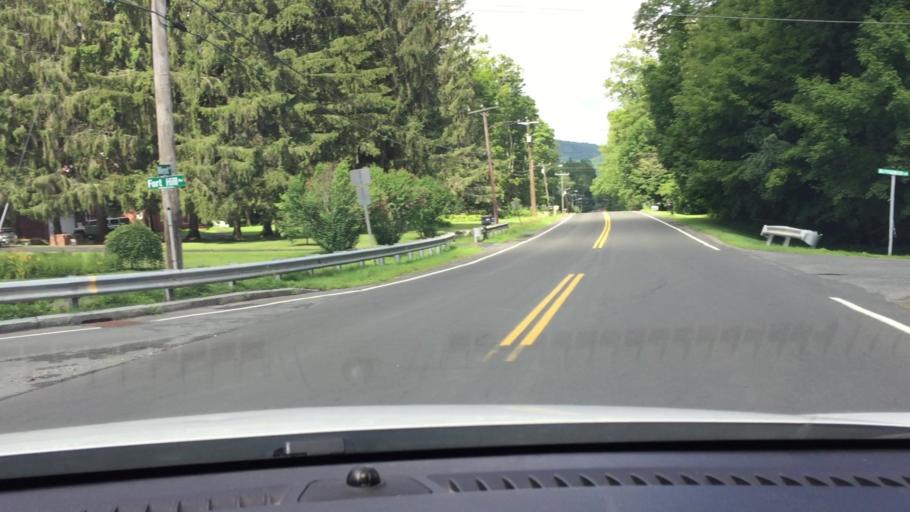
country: US
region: Massachusetts
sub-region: Berkshire County
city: Pittsfield
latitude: 42.4551
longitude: -73.2981
